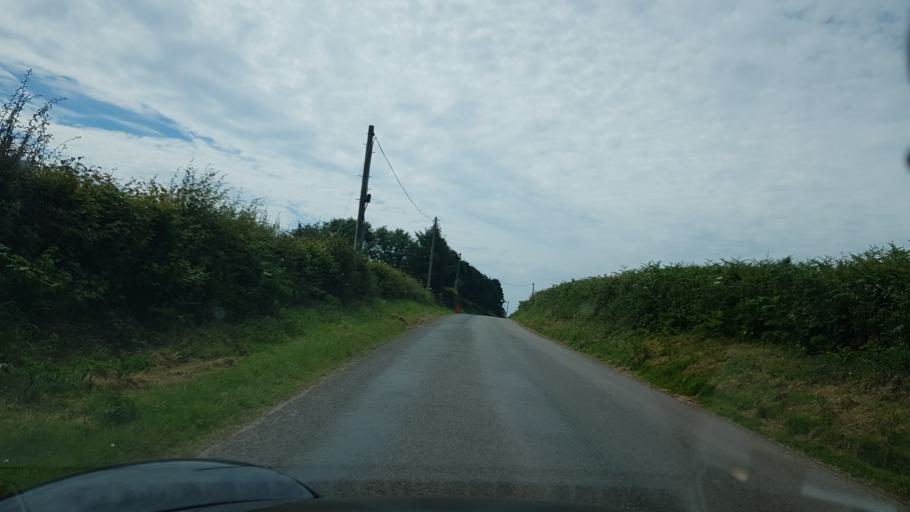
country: GB
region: Wales
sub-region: Carmarthenshire
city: Llanddowror
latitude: 51.7644
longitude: -4.5515
